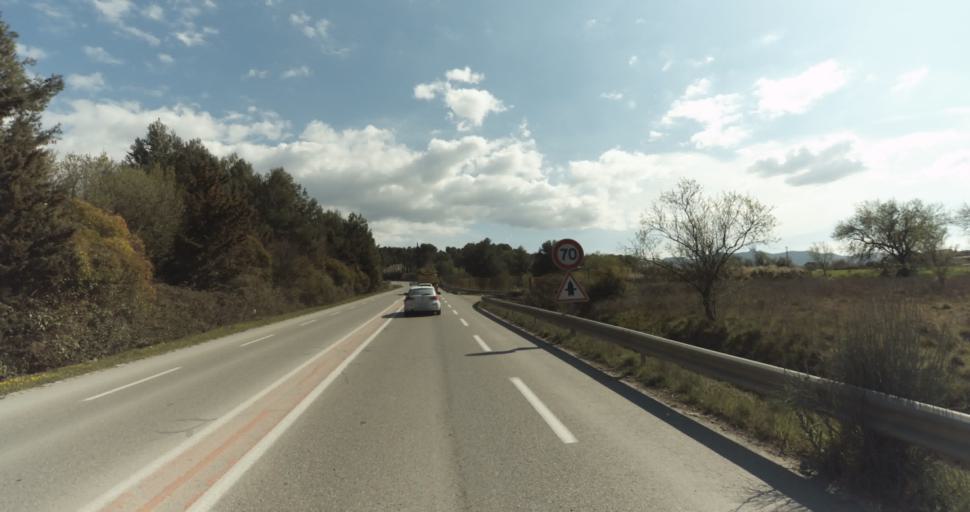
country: FR
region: Provence-Alpes-Cote d'Azur
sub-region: Departement des Bouches-du-Rhone
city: Gardanne
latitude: 43.4608
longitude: 5.4887
